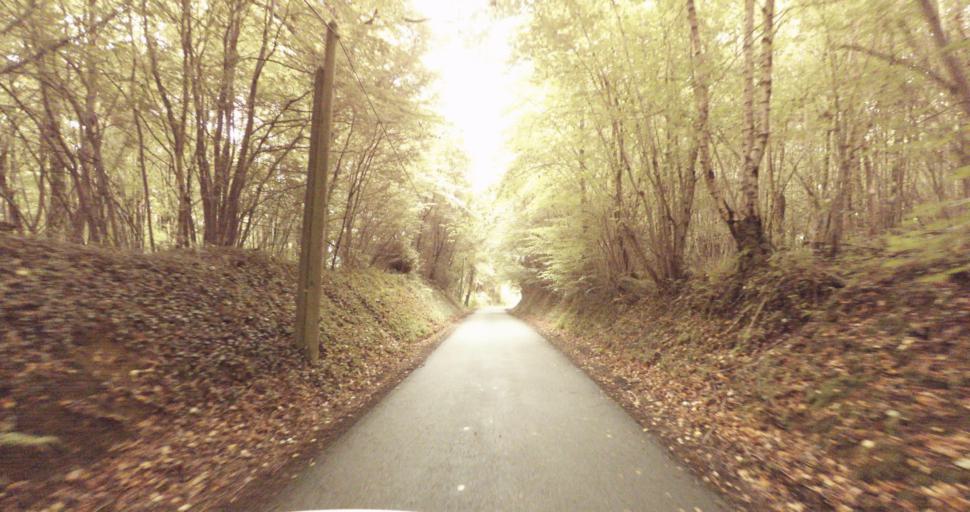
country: FR
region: Lower Normandy
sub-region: Departement de l'Orne
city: Trun
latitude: 48.9282
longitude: 0.0708
